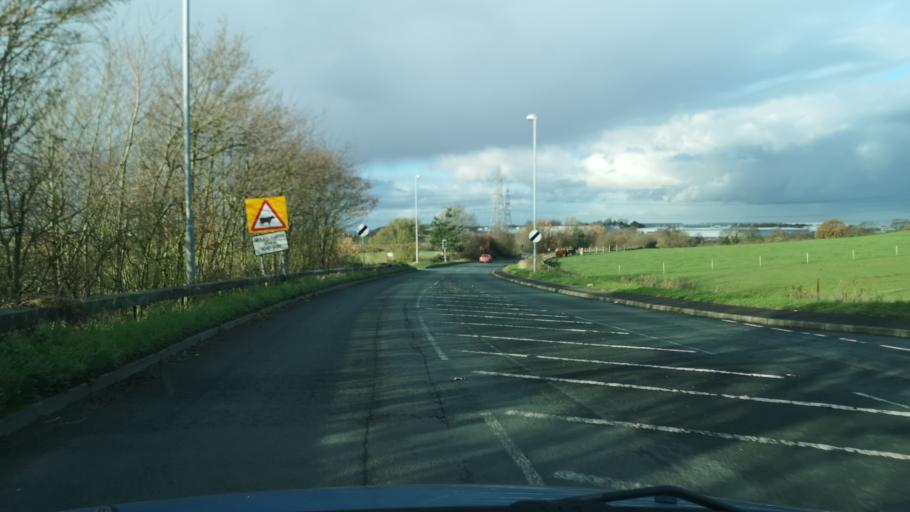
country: GB
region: England
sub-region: City and Borough of Wakefield
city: Featherstone
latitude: 53.6907
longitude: -1.3802
